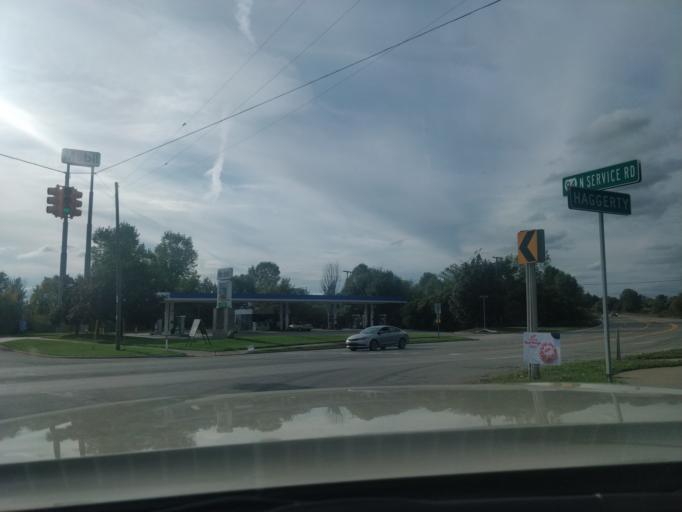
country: US
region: Michigan
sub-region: Wayne County
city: Romulus
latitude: 42.2225
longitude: -83.4401
